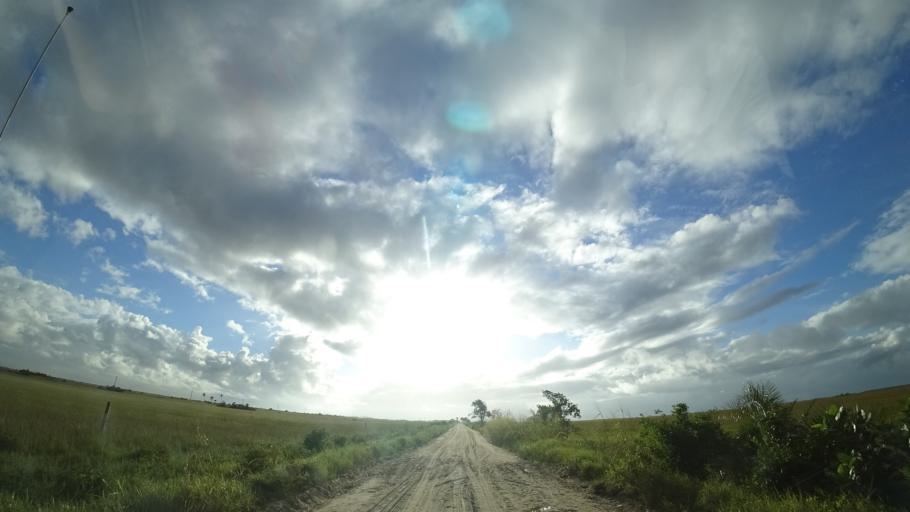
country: MZ
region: Sofala
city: Beira
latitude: -19.7559
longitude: 34.9243
